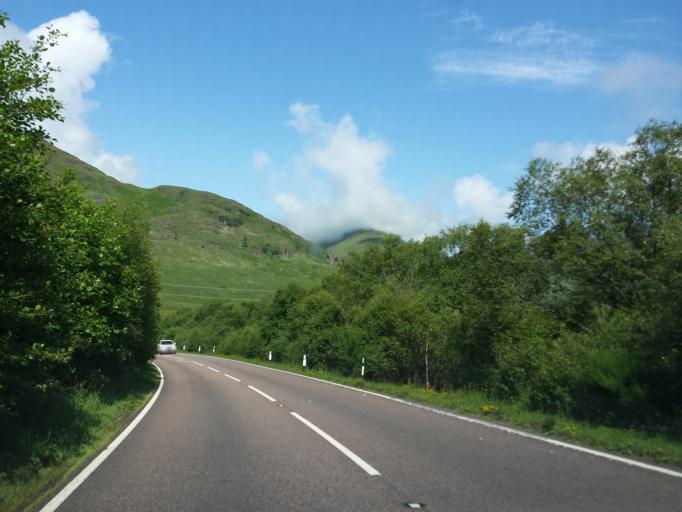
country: GB
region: Scotland
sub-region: Argyll and Bute
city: Garelochhead
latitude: 56.4100
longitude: -5.0223
